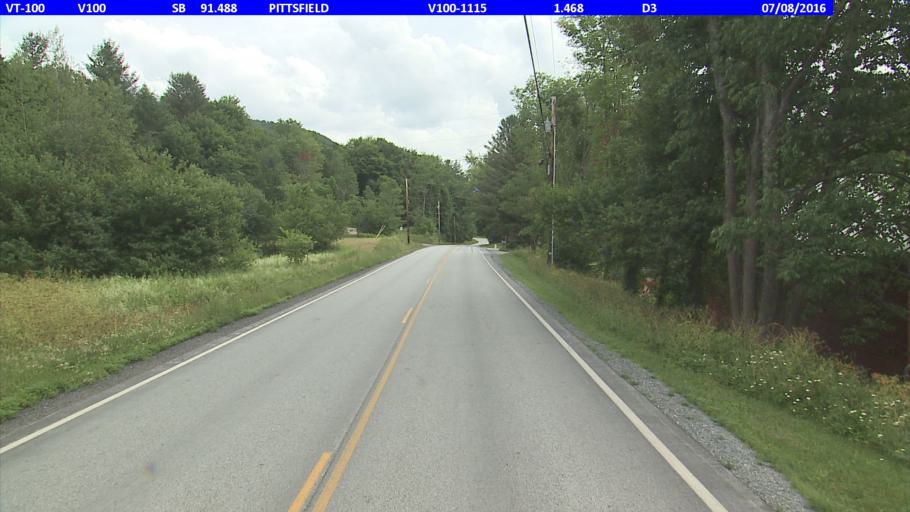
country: US
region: Vermont
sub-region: Rutland County
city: Rutland
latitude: 43.7383
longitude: -72.8204
